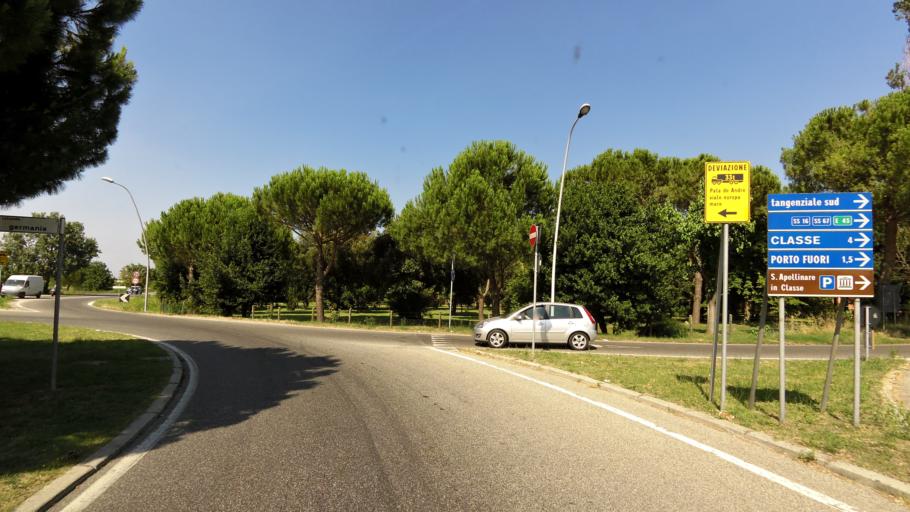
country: IT
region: Emilia-Romagna
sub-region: Provincia di Ravenna
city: Porto Fuori
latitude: 44.4103
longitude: 12.2306
